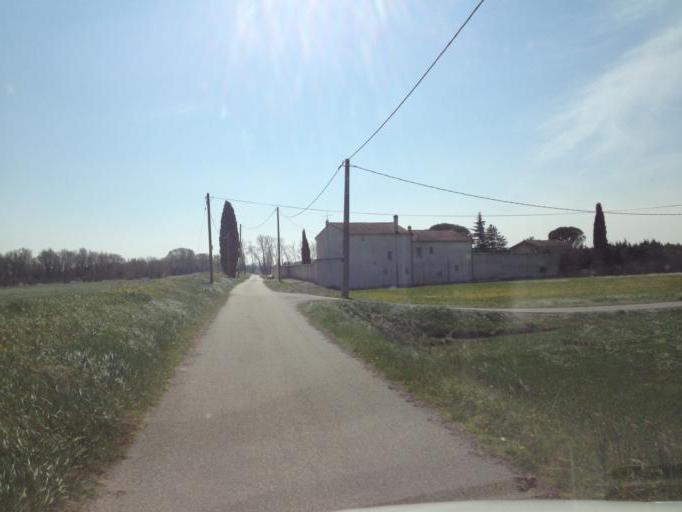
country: FR
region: Provence-Alpes-Cote d'Azur
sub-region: Departement du Vaucluse
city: Bedarrides
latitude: 44.0617
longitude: 4.9286
